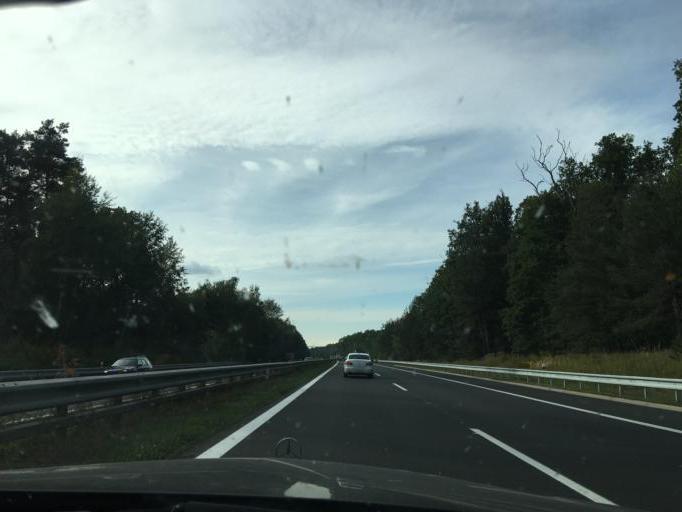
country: CZ
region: Central Bohemia
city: Poricany
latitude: 50.1229
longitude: 14.9298
